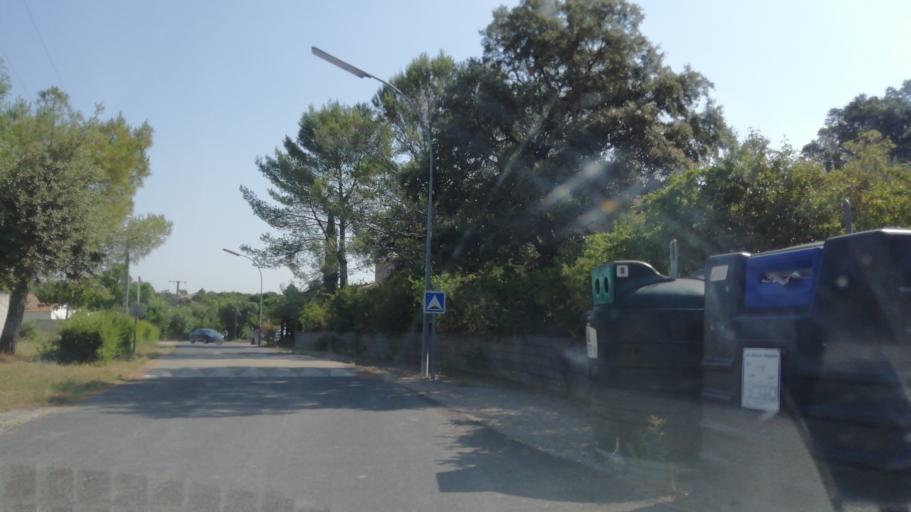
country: FR
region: Languedoc-Roussillon
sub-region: Departement de l'Herault
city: Saint-Mathieu-de-Treviers
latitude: 43.7401
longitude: 3.8553
